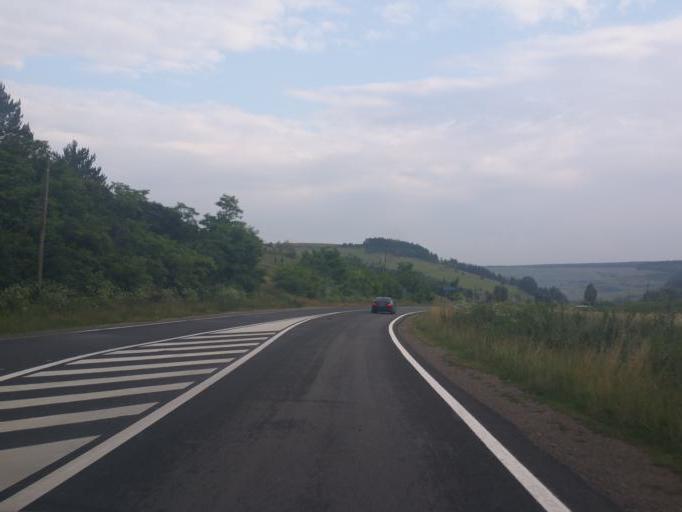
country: RO
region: Cluj
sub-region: Comuna Sanpaul
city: Sanpaul
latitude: 46.8542
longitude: 23.4068
